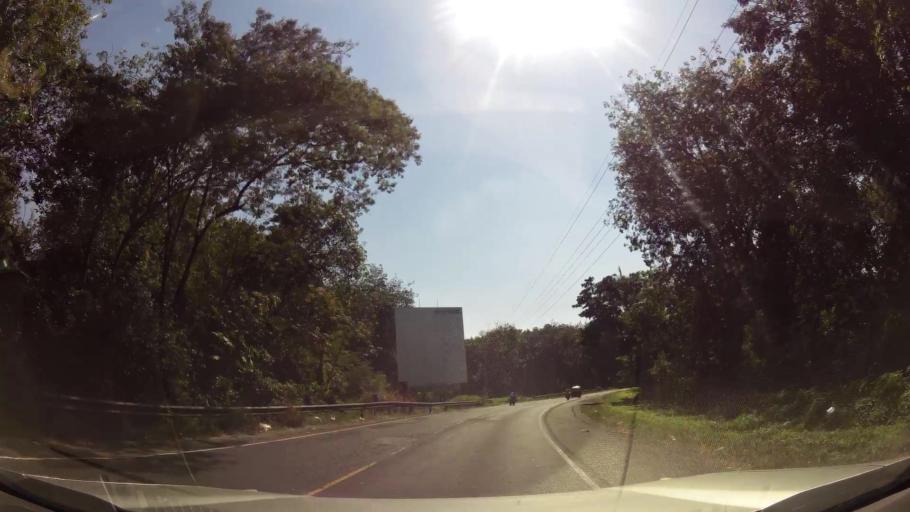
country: GT
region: Suchitepeque
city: Mazatenango
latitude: 14.5412
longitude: -91.4988
